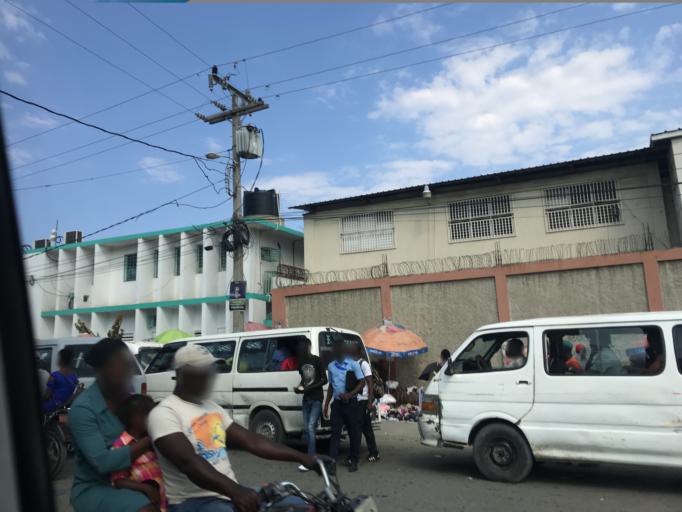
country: HT
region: Nord
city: Okap
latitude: 19.7535
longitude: -72.2061
